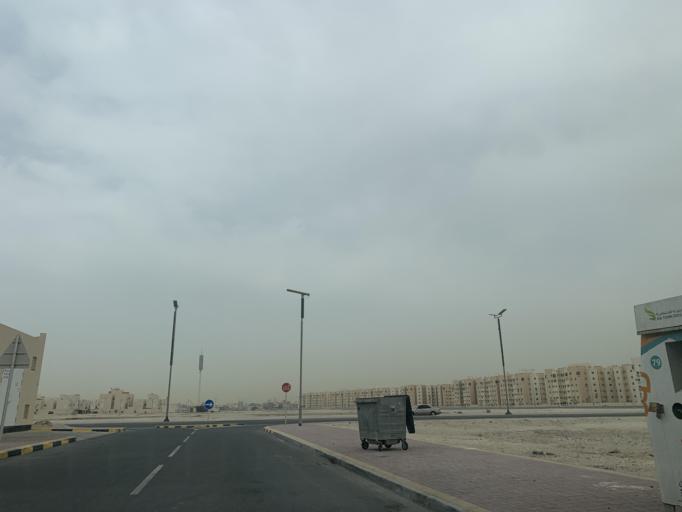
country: BH
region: Northern
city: Madinat `Isa
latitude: 26.1705
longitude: 50.5162
